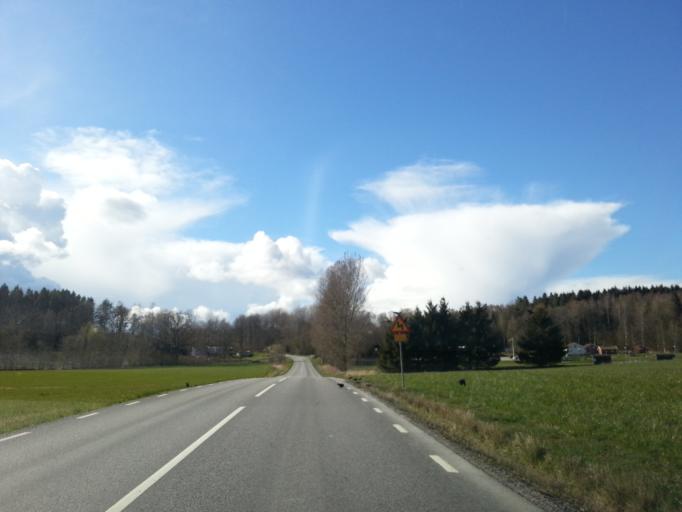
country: SE
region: Vaestra Goetaland
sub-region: Ale Kommun
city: Nodinge-Nol
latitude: 57.9354
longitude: 12.0413
